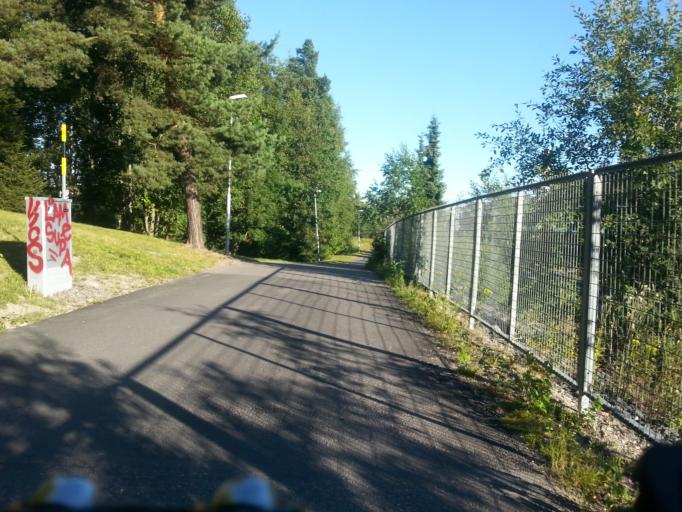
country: FI
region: Uusimaa
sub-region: Helsinki
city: Helsinki
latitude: 60.2114
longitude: 24.9143
